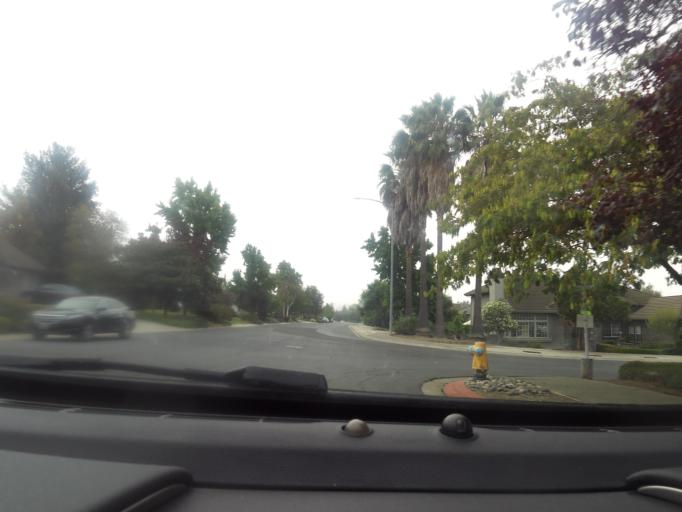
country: US
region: California
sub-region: San Benito County
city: Ridgemark
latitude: 36.8221
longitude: -121.3645
